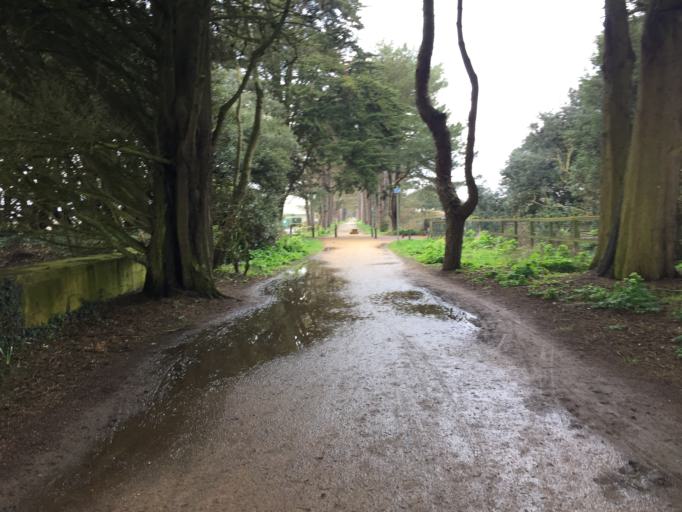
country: JE
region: St Helier
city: Saint Helier
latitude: 49.1894
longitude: -2.2163
